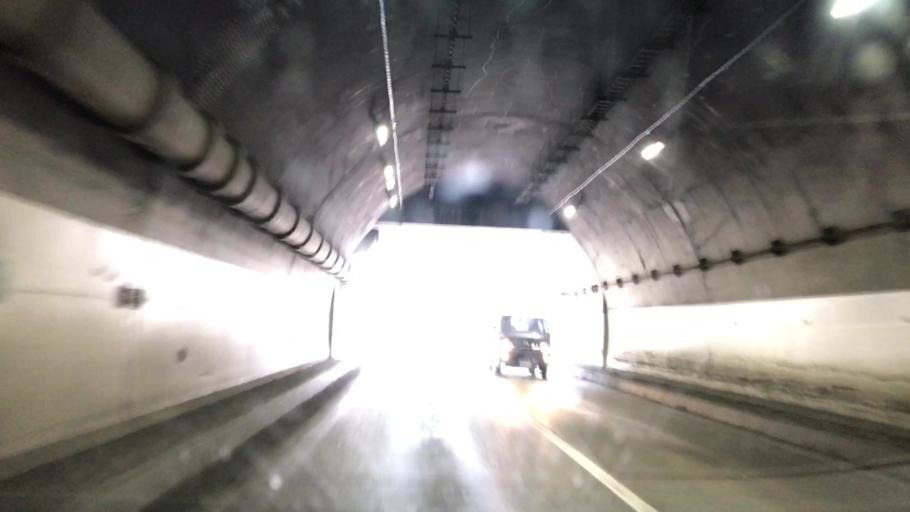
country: JP
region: Hokkaido
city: Shimo-furano
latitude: 42.8828
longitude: 142.4305
